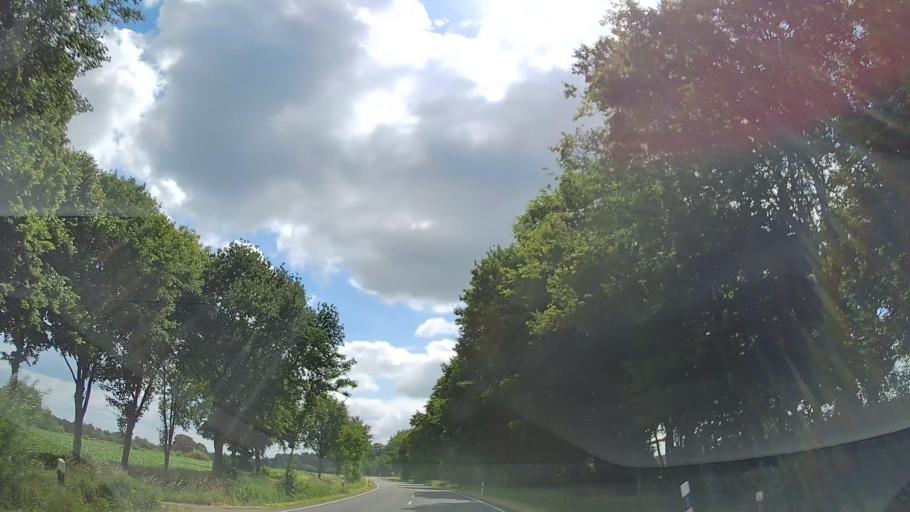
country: DE
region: Lower Saxony
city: Vechta
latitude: 52.6913
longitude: 8.3093
